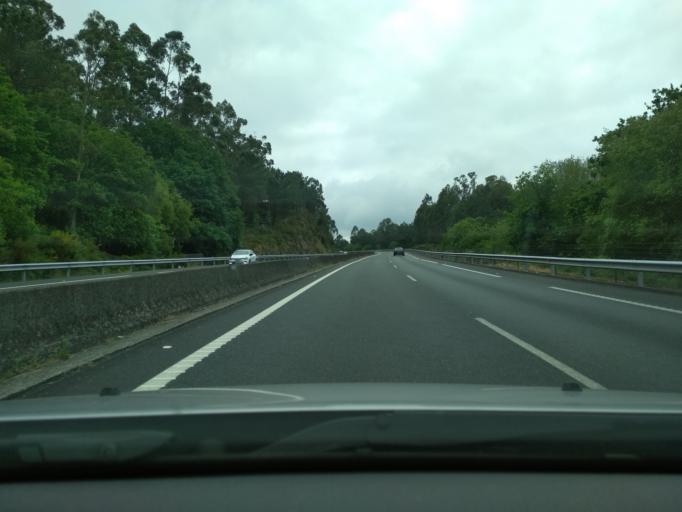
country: ES
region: Galicia
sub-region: Provincia da Coruna
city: Santiago de Compostela
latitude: 42.8482
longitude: -8.5715
